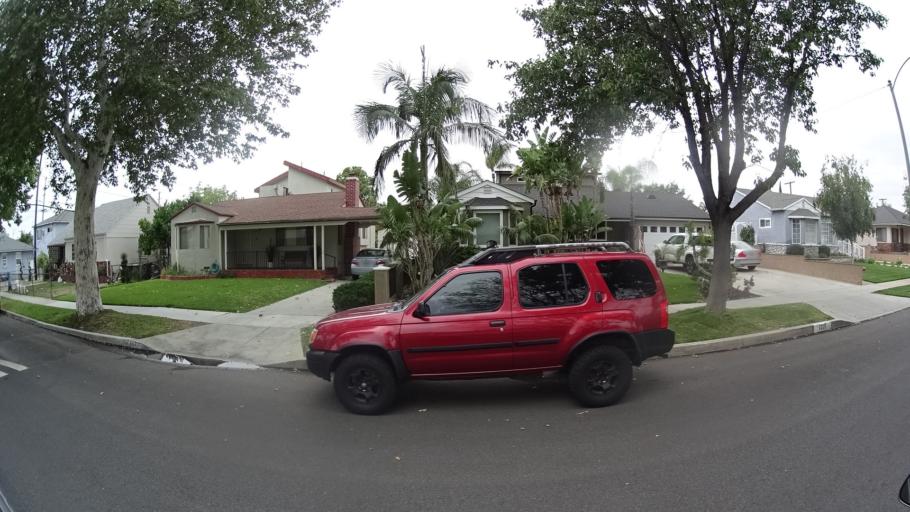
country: US
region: California
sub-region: Los Angeles County
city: Burbank
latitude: 34.1852
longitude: -118.3295
